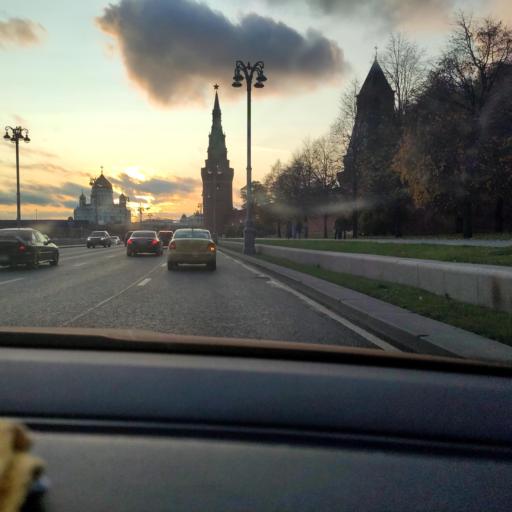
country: RU
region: Moscow
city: Moscow
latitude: 55.7490
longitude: 37.6161
